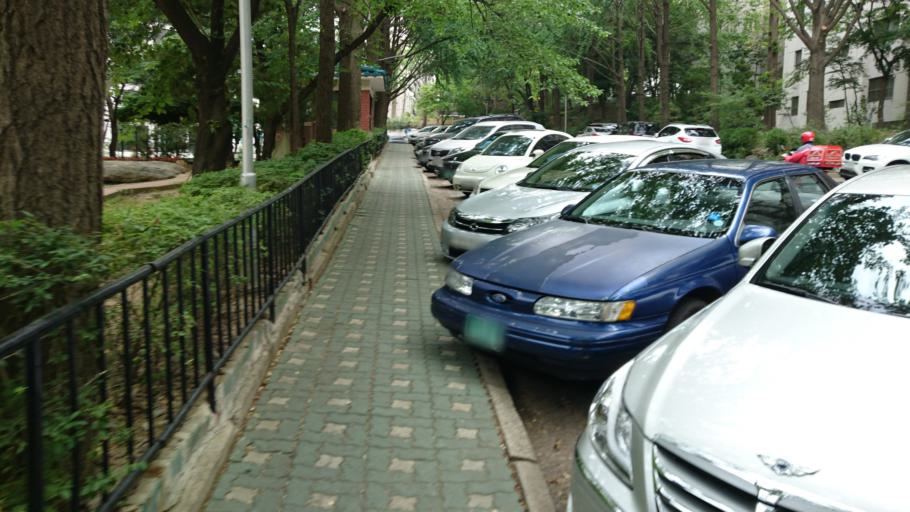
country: KR
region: Seoul
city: Seoul
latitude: 37.5293
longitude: 126.9942
